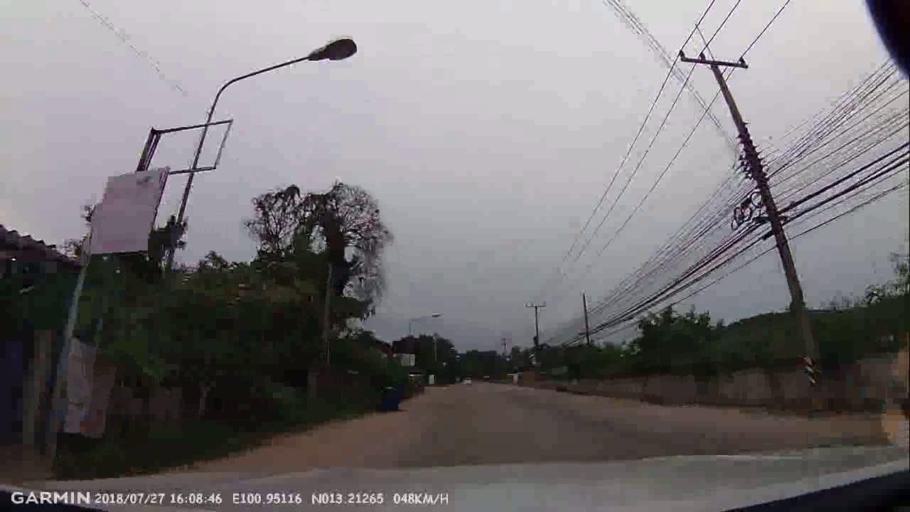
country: TH
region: Chon Buri
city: Si Racha
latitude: 13.2127
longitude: 100.9513
